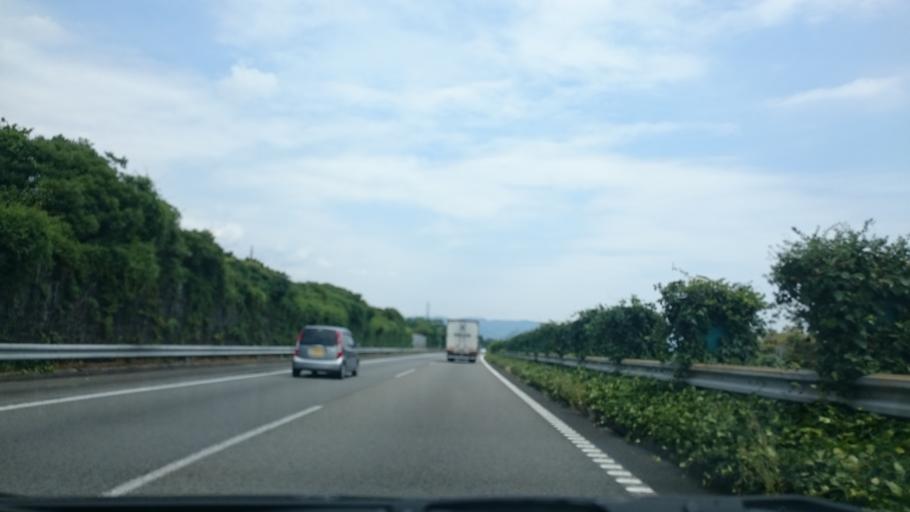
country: JP
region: Shizuoka
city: Shizuoka-shi
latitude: 35.0210
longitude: 138.4426
